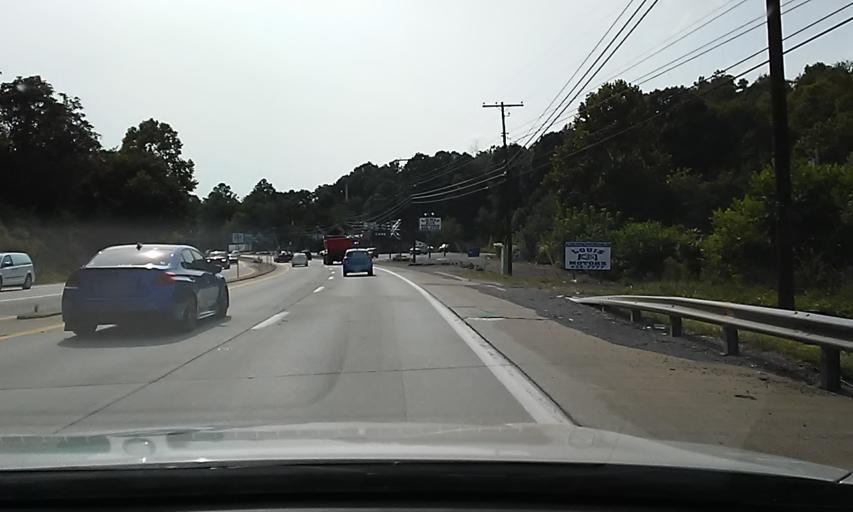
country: US
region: Pennsylvania
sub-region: Fayette County
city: Connellsville
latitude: 40.0469
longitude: -79.5694
